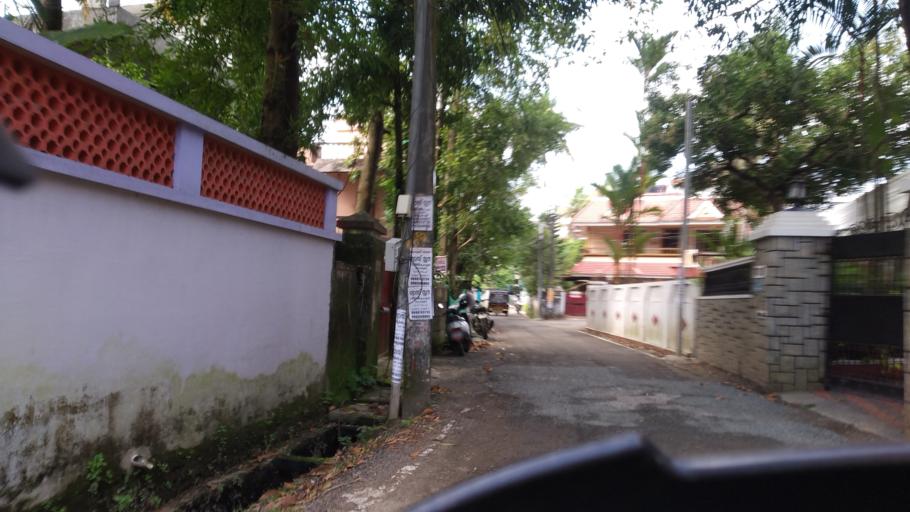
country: IN
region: Kerala
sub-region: Ernakulam
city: Cochin
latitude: 9.9852
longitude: 76.2999
